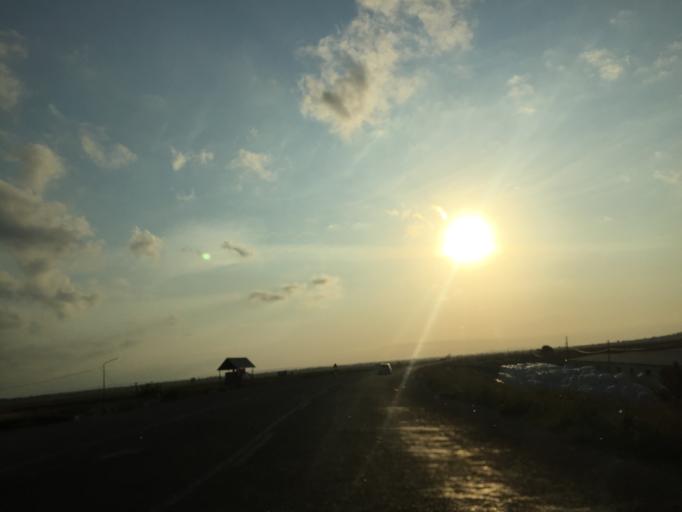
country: TR
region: Balikesir
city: Sevketiye
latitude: 40.1208
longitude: 27.8655
